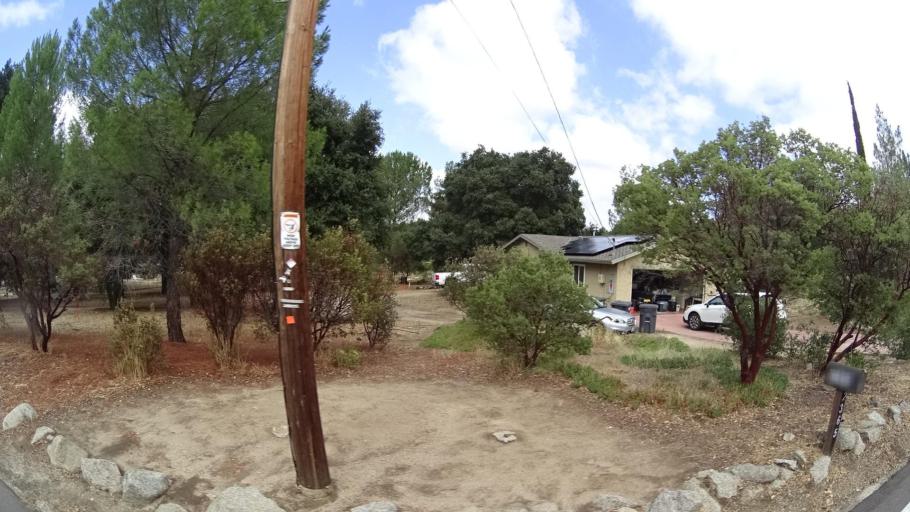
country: US
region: California
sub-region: San Diego County
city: Campo
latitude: 32.6777
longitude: -116.5088
